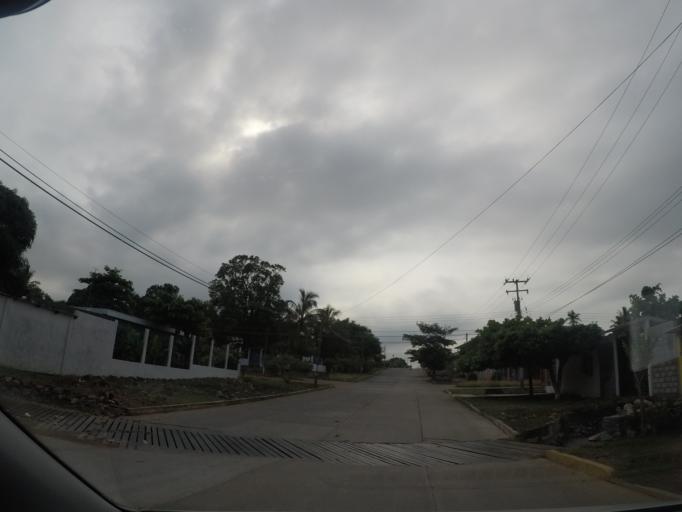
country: MX
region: Oaxaca
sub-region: Santa Maria Petapa
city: Llano Suchiapa
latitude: 16.8713
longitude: -95.0486
